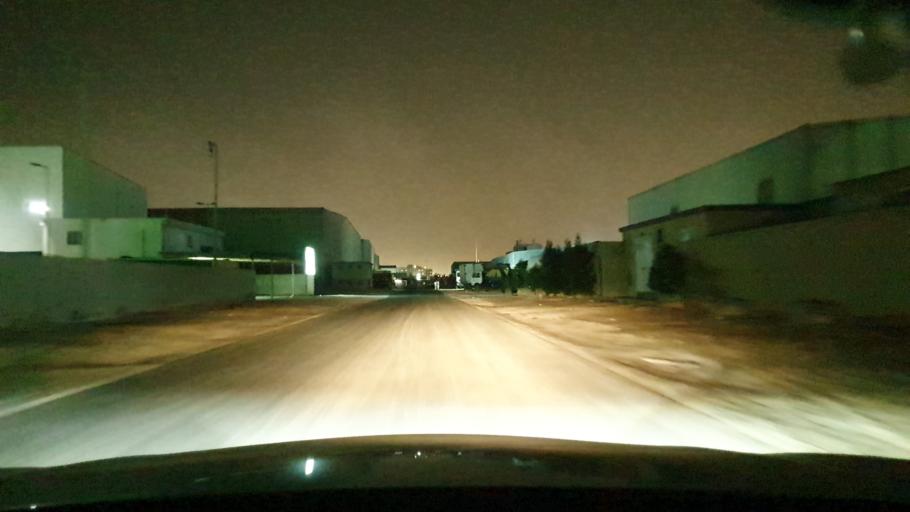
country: BH
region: Northern
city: Sitrah
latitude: 26.0973
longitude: 50.6216
